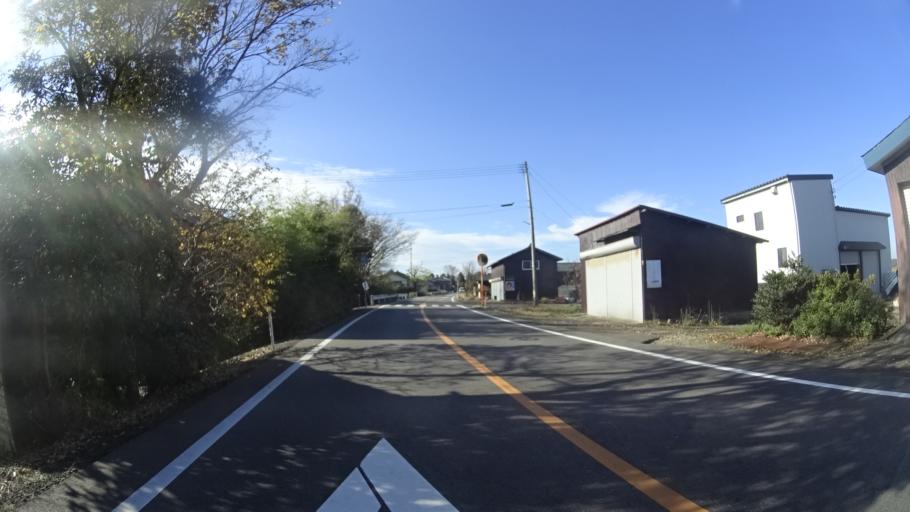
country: JP
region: Niigata
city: Yoshida-kasugacho
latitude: 37.5961
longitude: 138.8472
